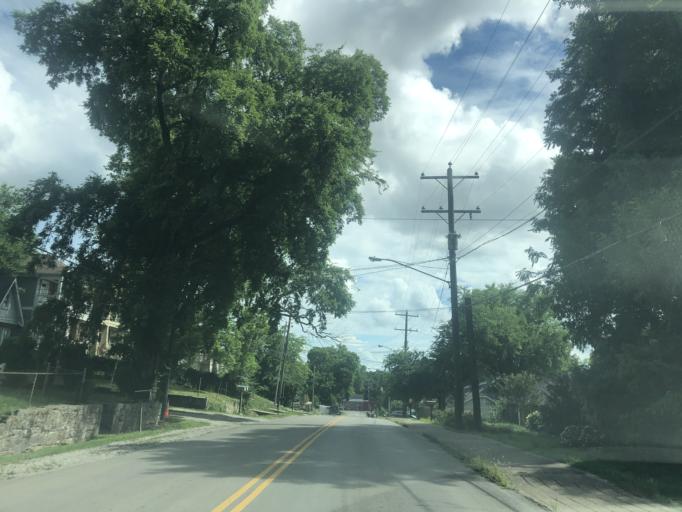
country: US
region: Tennessee
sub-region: Davidson County
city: Nashville
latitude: 36.1966
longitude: -86.7671
